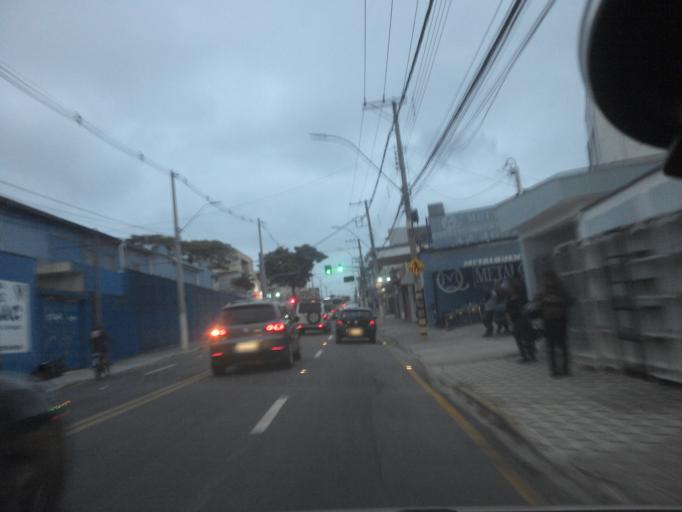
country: BR
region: Sao Paulo
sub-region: Taubate
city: Taubate
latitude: -23.0224
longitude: -45.5477
